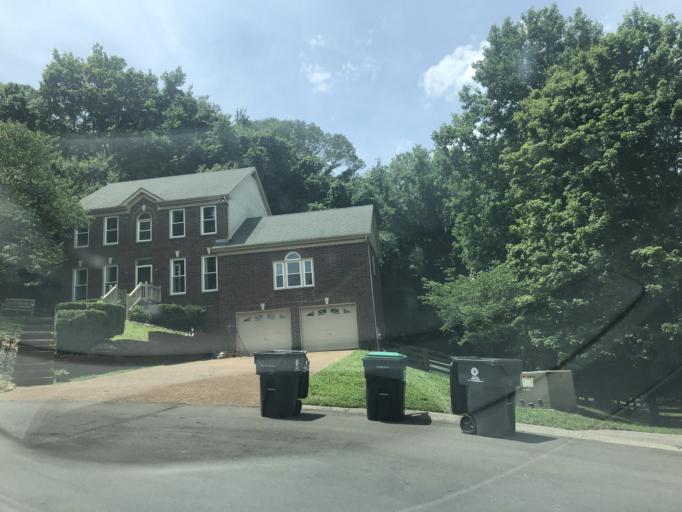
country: US
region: Tennessee
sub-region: Cheatham County
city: Pegram
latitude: 36.0533
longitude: -86.9573
